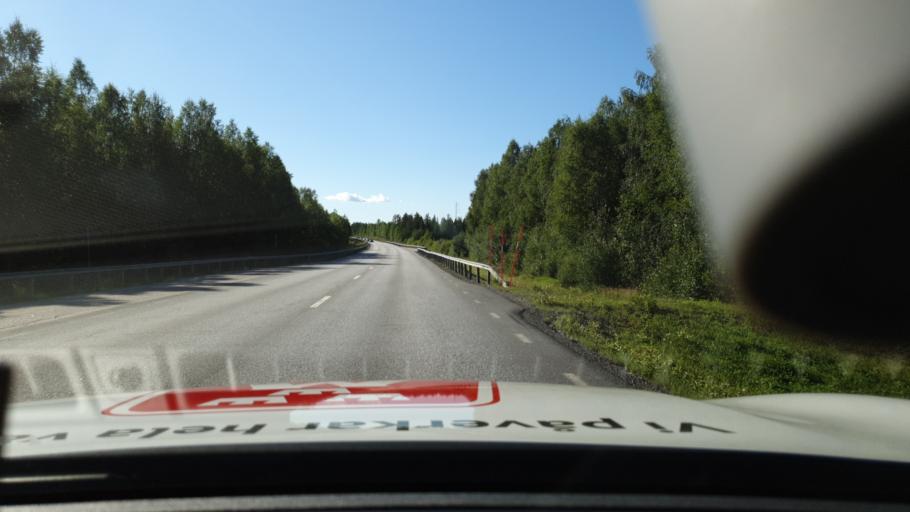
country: SE
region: Norrbotten
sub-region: Pitea Kommun
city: Rosvik
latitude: 65.5936
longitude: 21.6421
